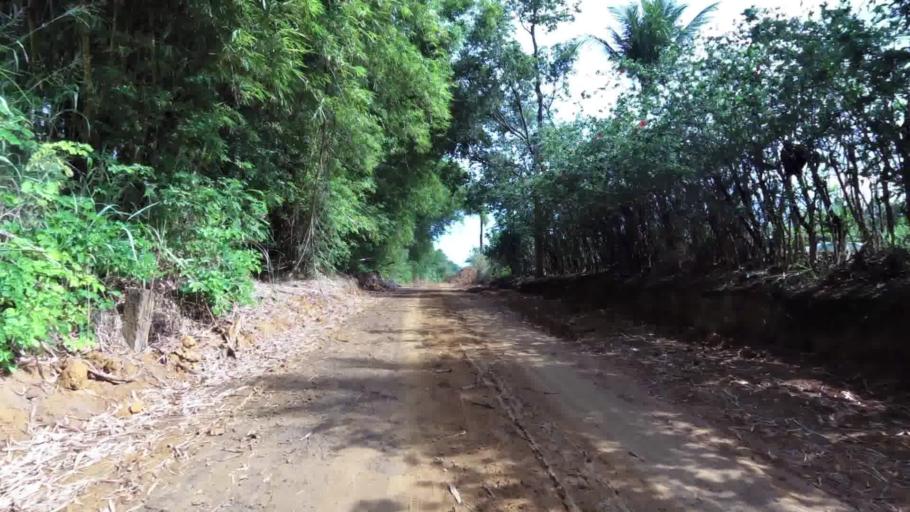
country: BR
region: Espirito Santo
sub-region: Piuma
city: Piuma
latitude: -20.8105
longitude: -40.6658
